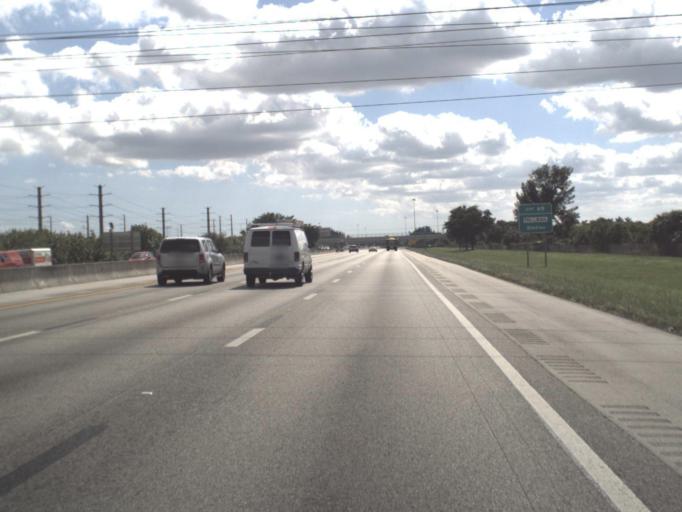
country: US
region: Florida
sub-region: Broward County
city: Coconut Creek
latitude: 26.2804
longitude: -80.1691
